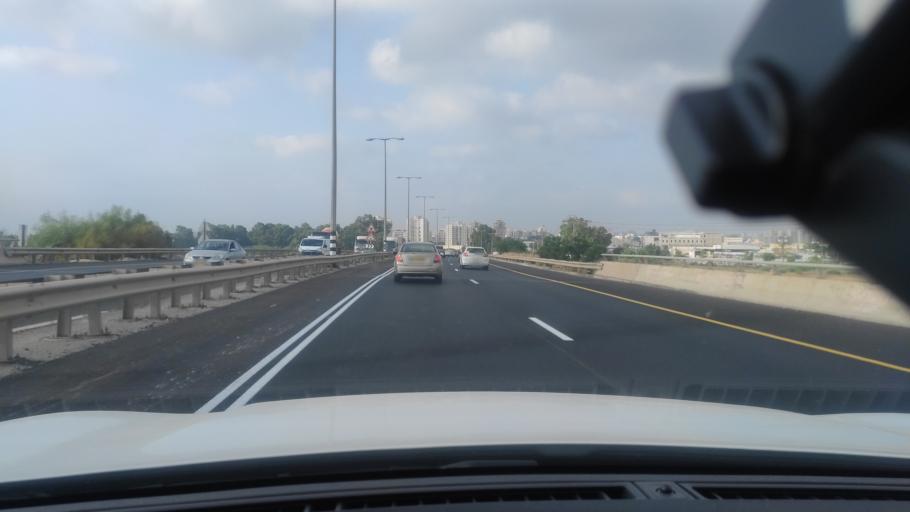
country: IL
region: Central District
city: Petah Tiqwa
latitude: 32.1117
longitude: 34.9026
